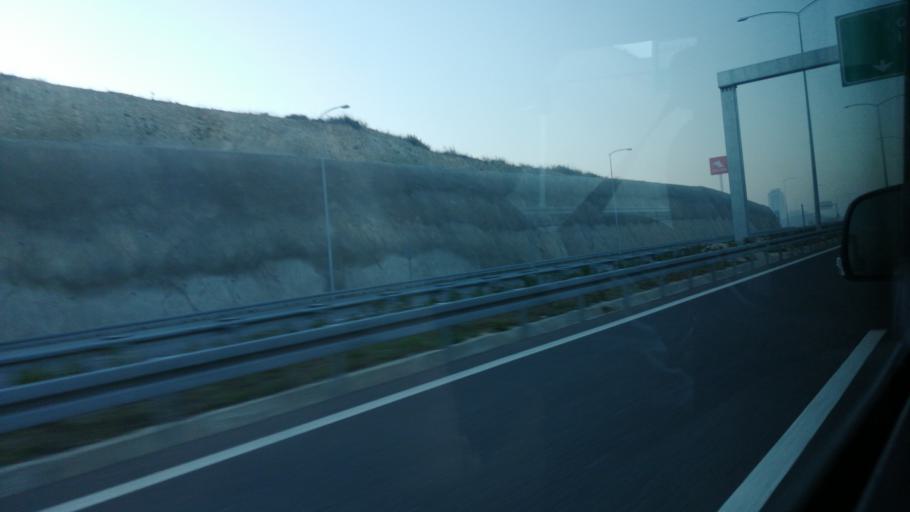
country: TR
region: Kocaeli
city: Tavsanli
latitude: 40.7791
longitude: 29.5179
